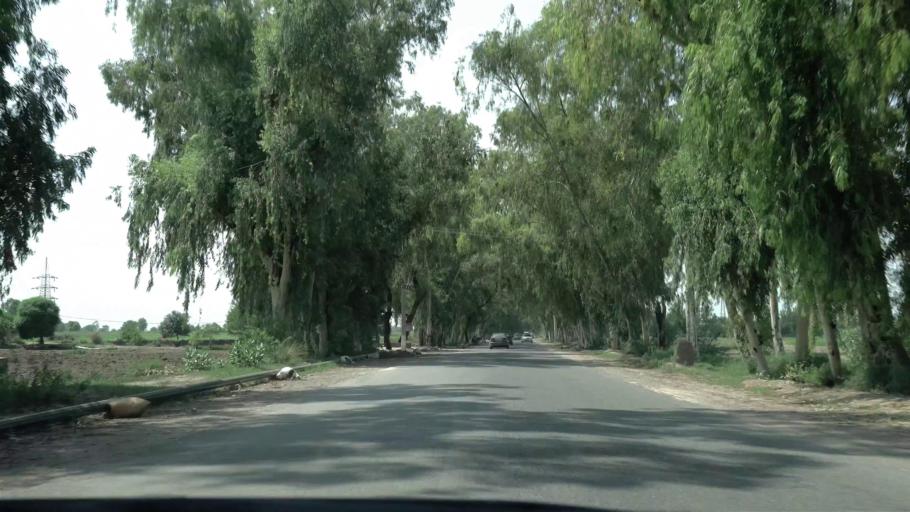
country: PK
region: Punjab
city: Gojra
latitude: 31.1705
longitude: 72.6198
